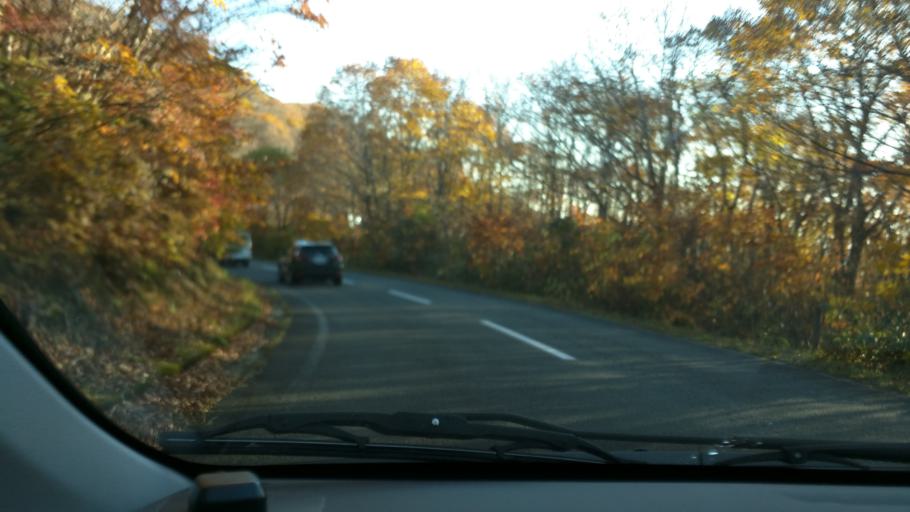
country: JP
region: Fukushima
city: Inawashiro
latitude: 37.6038
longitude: 140.0522
